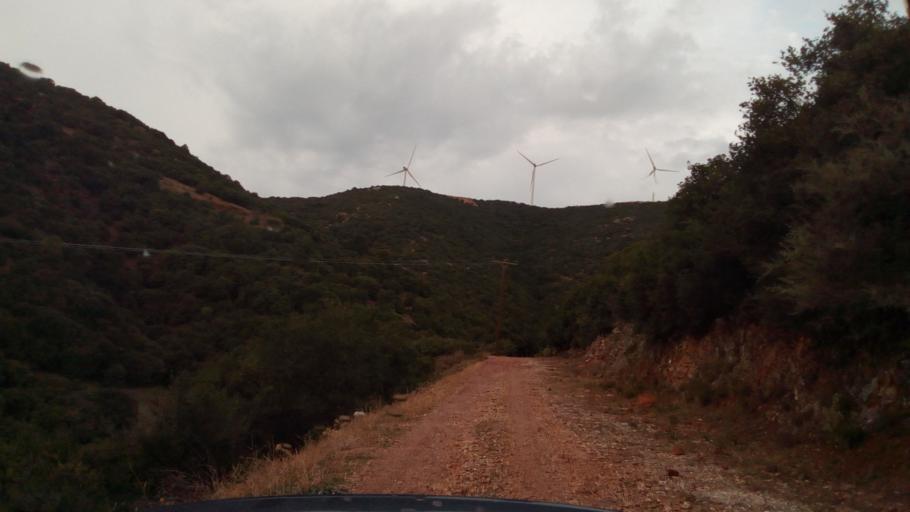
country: GR
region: West Greece
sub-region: Nomos Achaias
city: Kamarai
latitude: 38.4132
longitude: 22.0527
